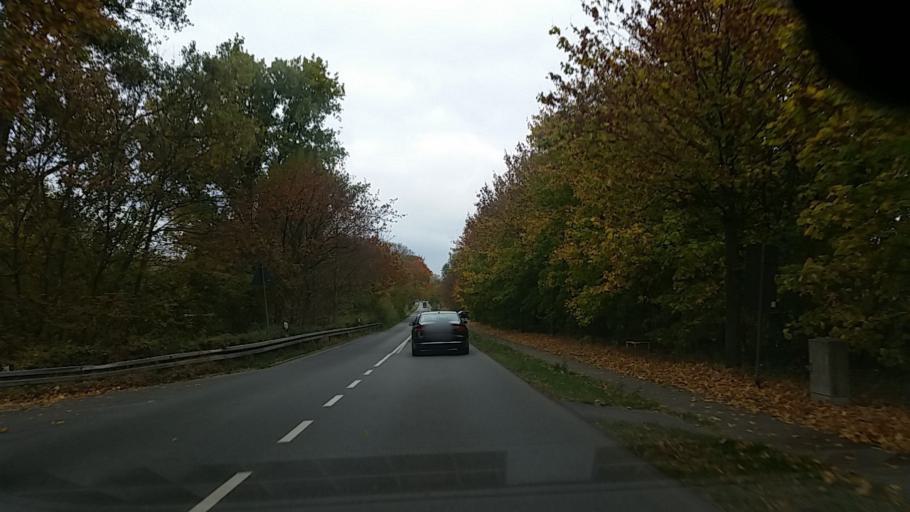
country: DE
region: Lower Saxony
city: Weyhausen
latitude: 52.4270
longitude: 10.7160
